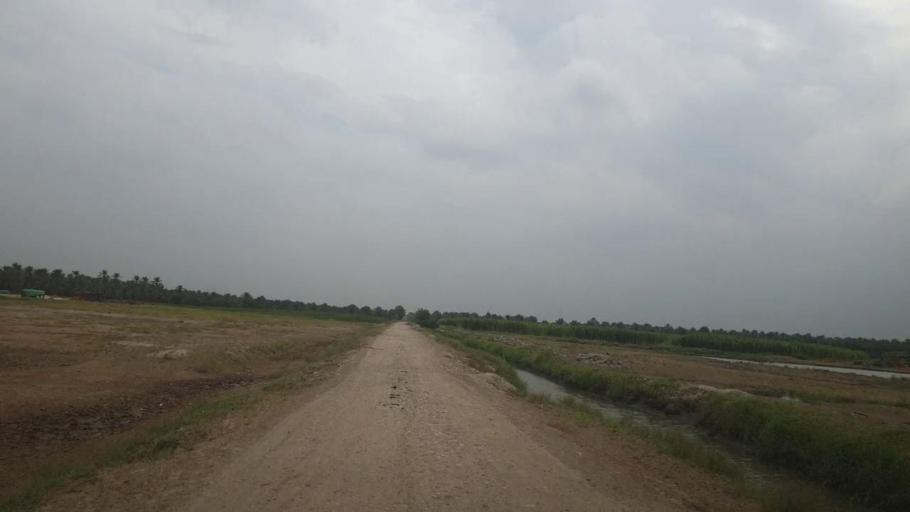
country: PK
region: Sindh
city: Khairpur
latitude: 27.5640
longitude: 68.7144
